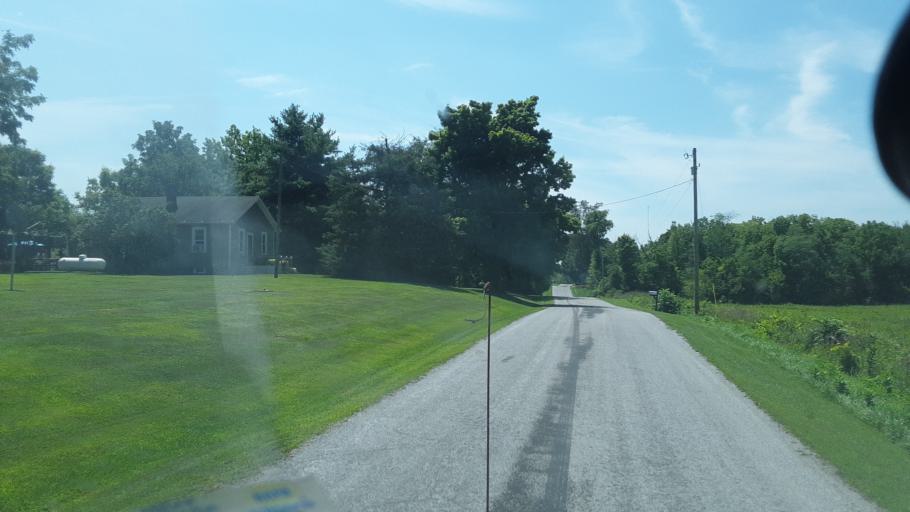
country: US
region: Ohio
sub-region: Hardin County
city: Forest
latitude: 40.7693
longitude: -83.5685
